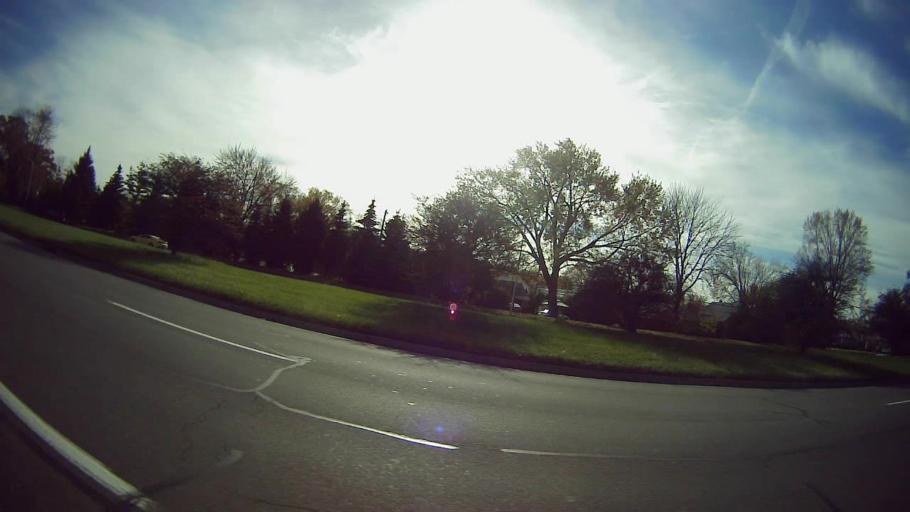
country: US
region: Michigan
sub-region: Wayne County
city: Dearborn Heights
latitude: 42.3272
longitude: -83.2569
